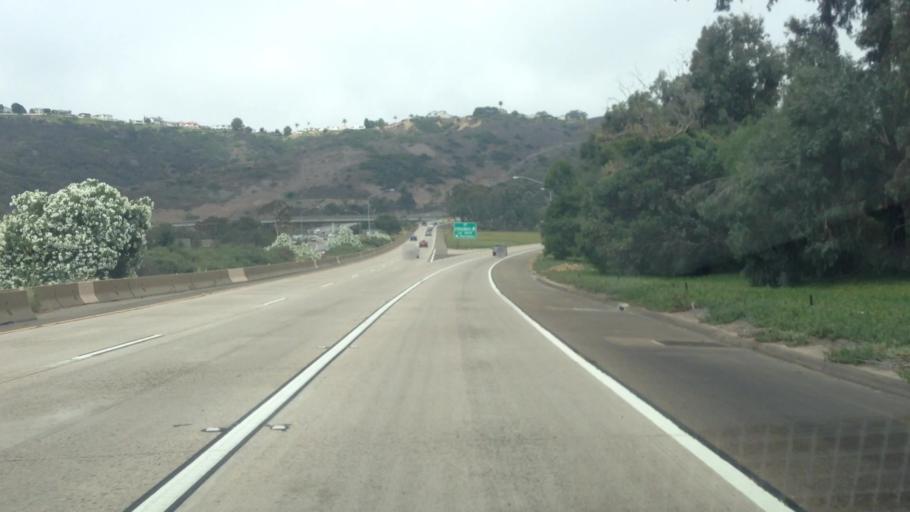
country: US
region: California
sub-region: San Diego County
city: La Jolla
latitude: 32.8392
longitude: -117.2286
